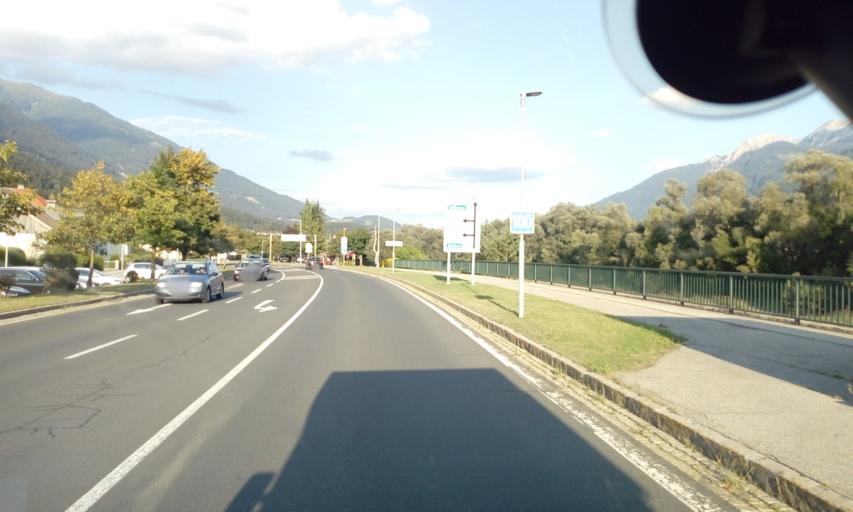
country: AT
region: Carinthia
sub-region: Politischer Bezirk Spittal an der Drau
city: Oberdrauburg
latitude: 46.7478
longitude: 12.9709
